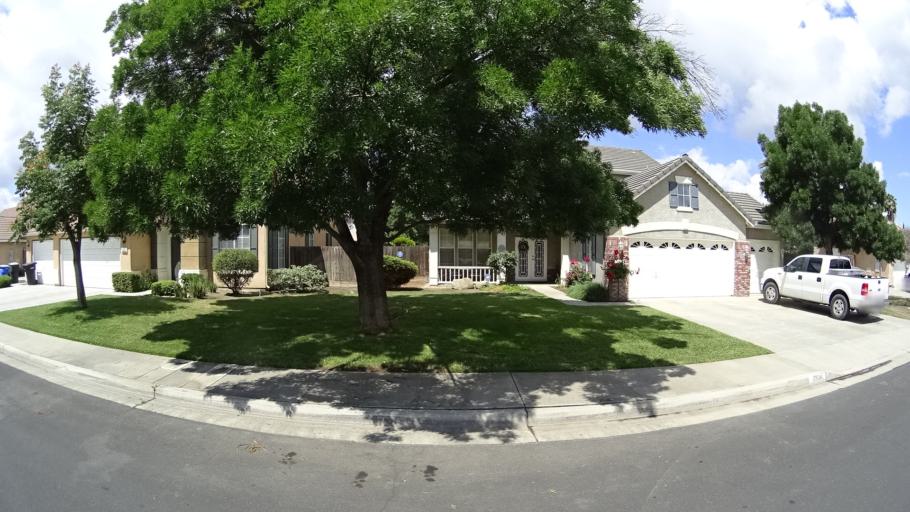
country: US
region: California
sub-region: Kings County
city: Lucerne
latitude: 36.3642
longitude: -119.6558
